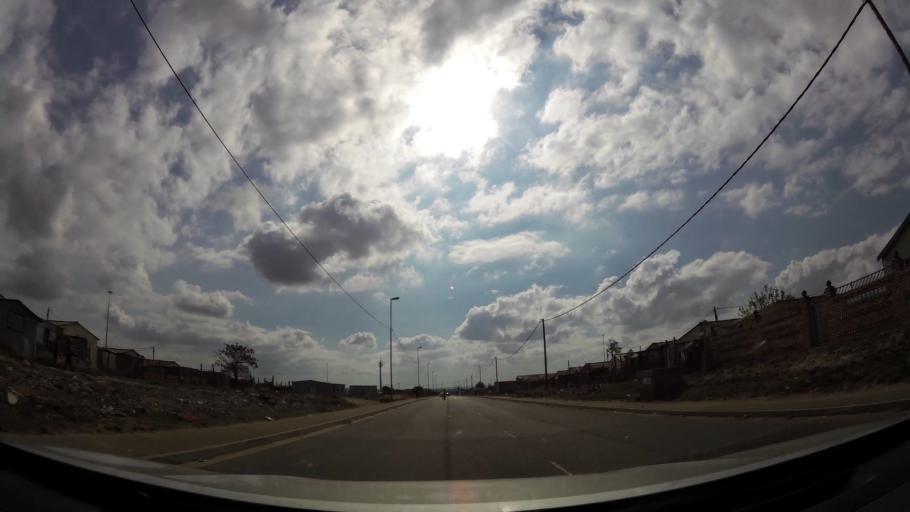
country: ZA
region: Eastern Cape
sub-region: Nelson Mandela Bay Metropolitan Municipality
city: Port Elizabeth
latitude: -33.7924
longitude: 25.5811
